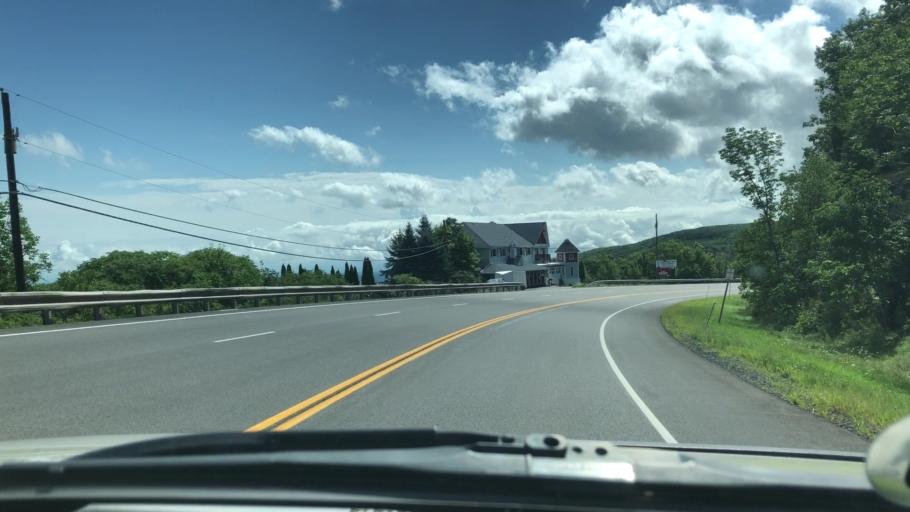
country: US
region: New York
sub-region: Greene County
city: Cairo
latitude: 42.3391
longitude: -74.1518
